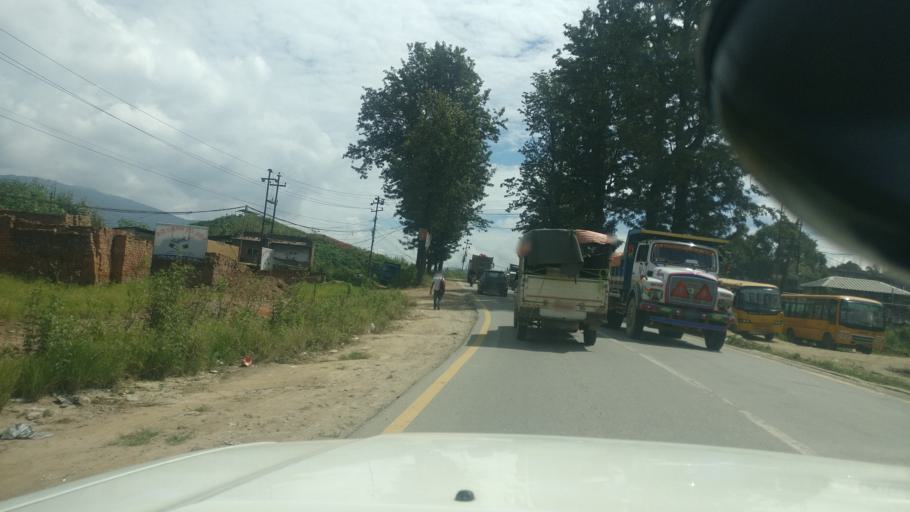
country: NP
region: Central Region
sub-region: Bagmati Zone
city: Bhaktapur
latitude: 27.6608
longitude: 85.4471
